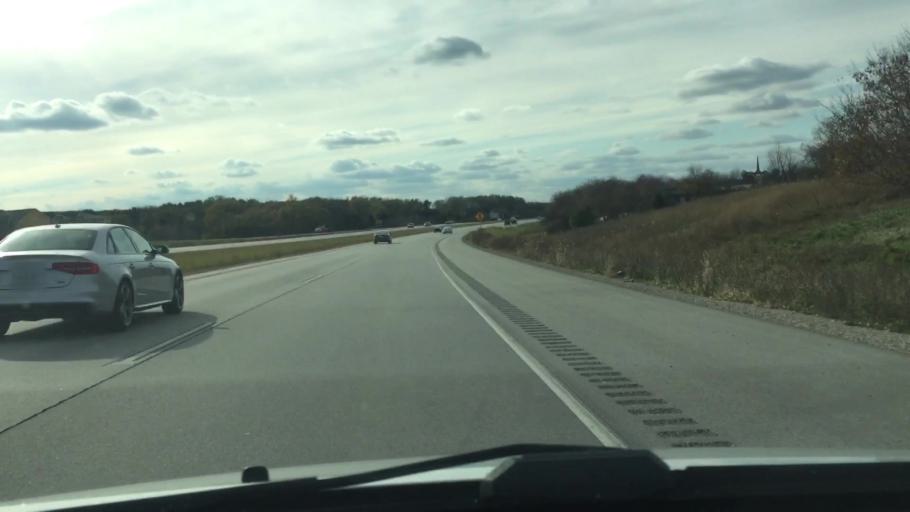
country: US
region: Wisconsin
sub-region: Waukesha County
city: Hartland
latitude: 43.1049
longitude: -88.3646
